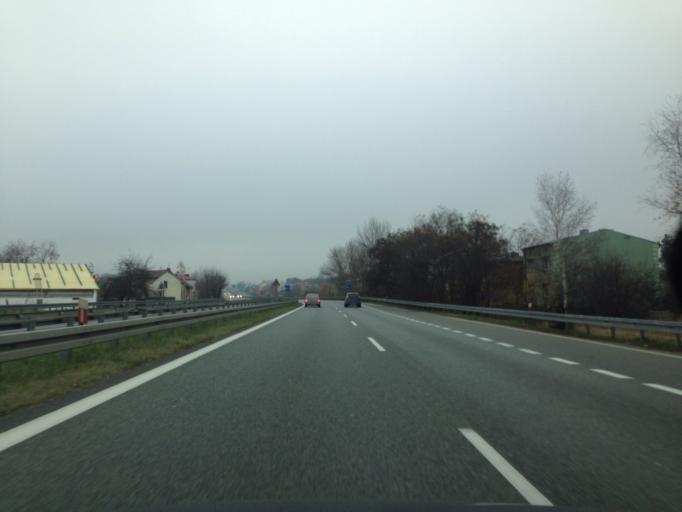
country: PL
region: Silesian Voivodeship
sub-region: Powiat bedzinski
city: Siewierz
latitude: 50.4740
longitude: 19.2283
